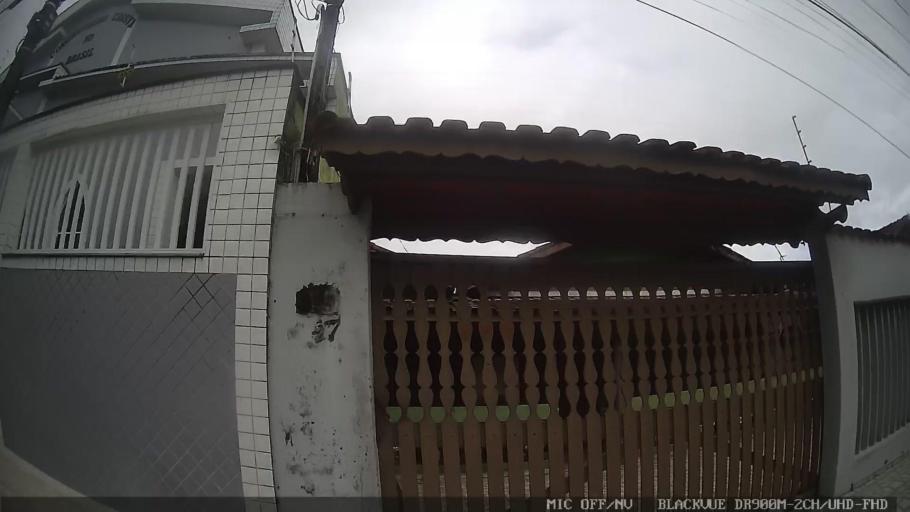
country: BR
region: Sao Paulo
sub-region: Itanhaem
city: Itanhaem
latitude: -24.1896
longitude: -46.8176
